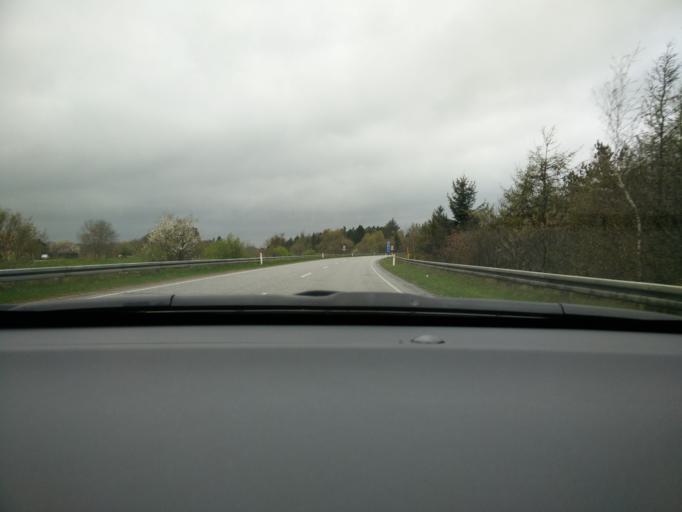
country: DK
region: Central Jutland
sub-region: Viborg Kommune
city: Viborg
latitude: 56.5038
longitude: 9.3312
